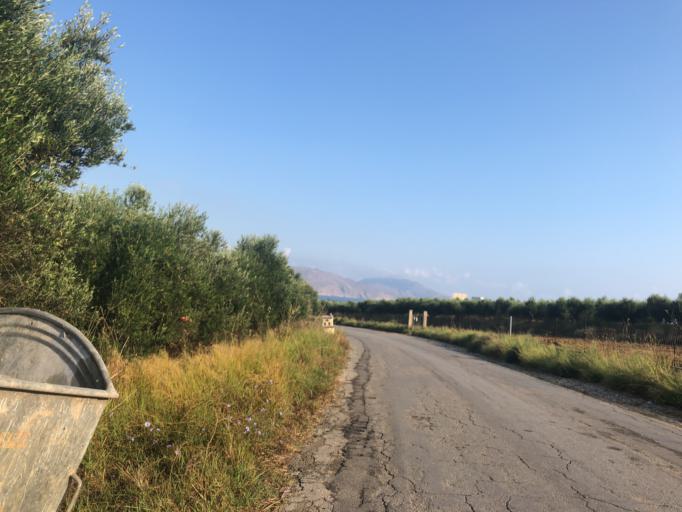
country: GR
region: Crete
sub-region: Nomos Chanias
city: Georgioupolis
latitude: 35.3475
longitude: 24.3076
